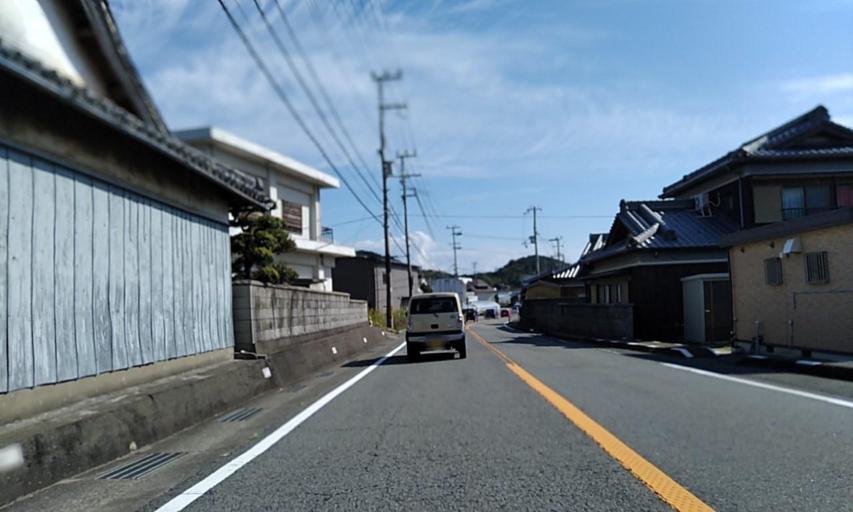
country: JP
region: Wakayama
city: Gobo
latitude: 33.8568
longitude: 135.1628
